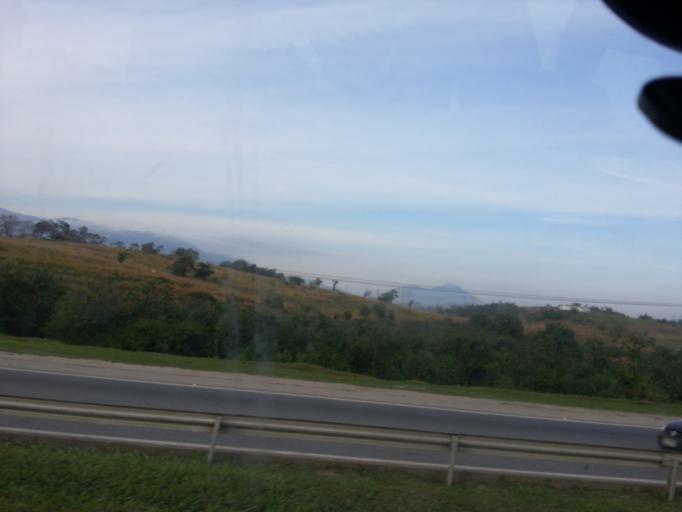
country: BR
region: Rio de Janeiro
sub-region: Queimados
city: Queimados
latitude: -22.7358
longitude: -43.5458
